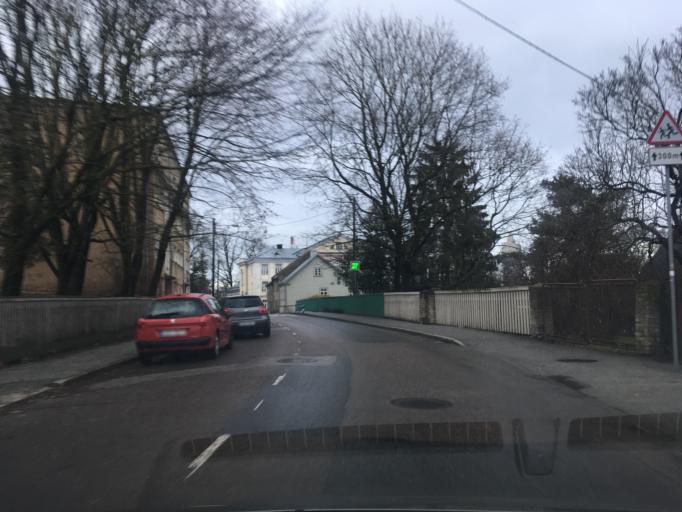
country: EE
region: Tartu
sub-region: Tartu linn
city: Tartu
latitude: 58.3702
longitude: 26.7343
